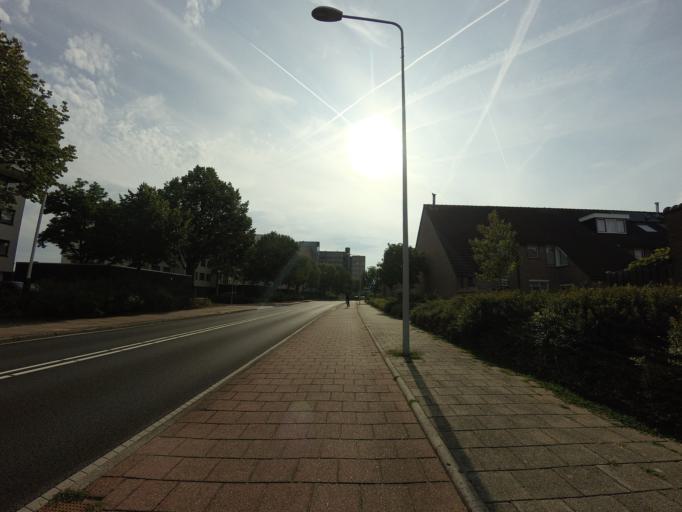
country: NL
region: South Holland
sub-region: Gemeente Papendrecht
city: Papendrecht
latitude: 51.8235
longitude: 4.6893
